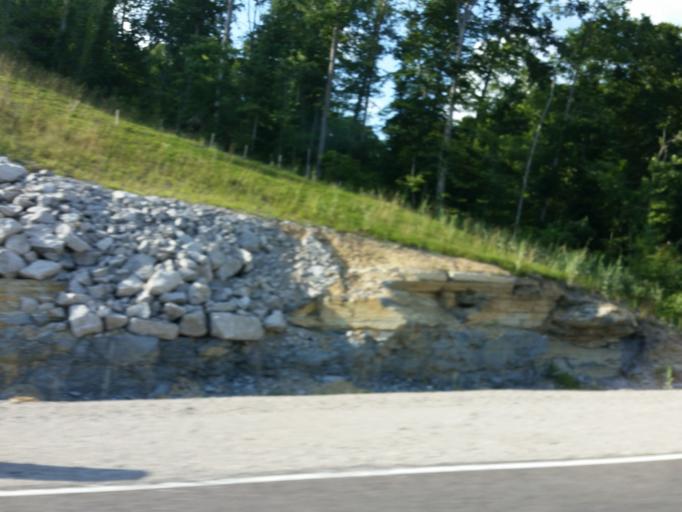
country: US
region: Tennessee
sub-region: Maury County
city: Mount Pleasant
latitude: 35.5646
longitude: -87.3574
